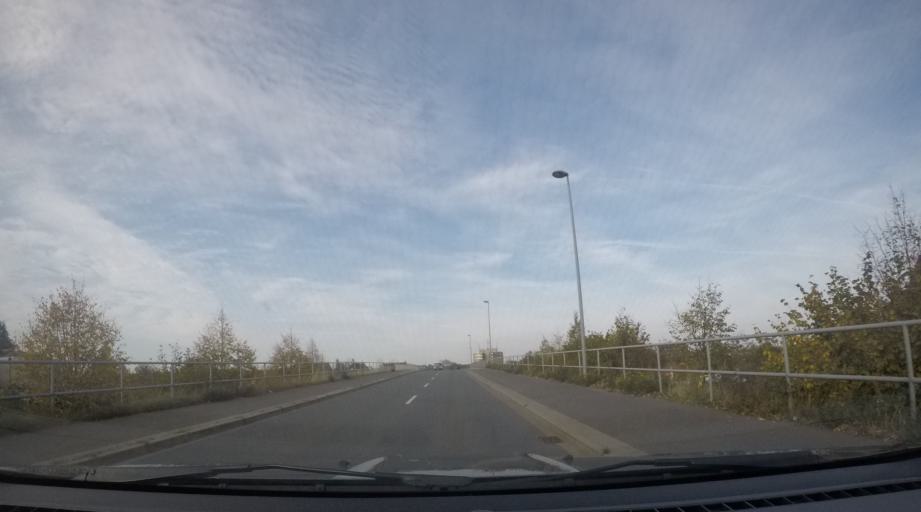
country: DE
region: North Rhine-Westphalia
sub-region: Regierungsbezirk Munster
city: Rhede
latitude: 51.8246
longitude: 6.6959
